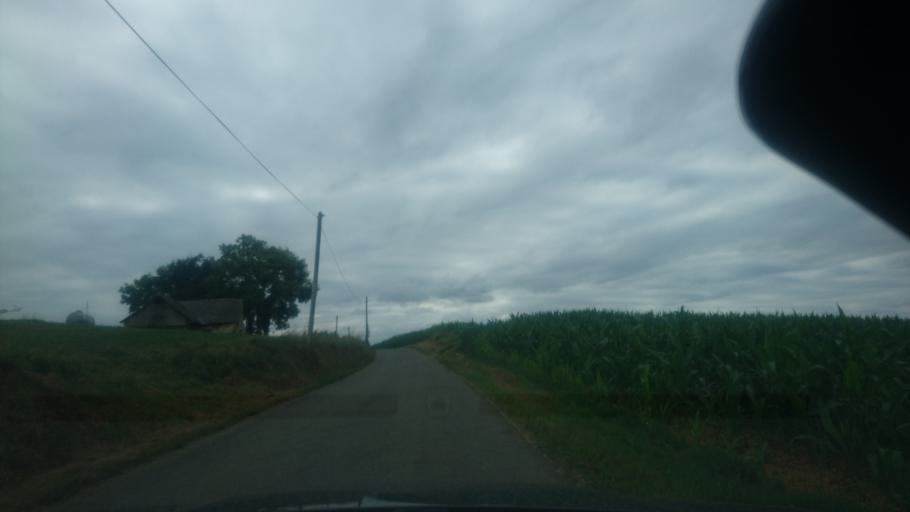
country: FR
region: Midi-Pyrenees
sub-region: Departement des Hautes-Pyrenees
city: Odos
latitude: 43.1351
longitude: 0.0508
